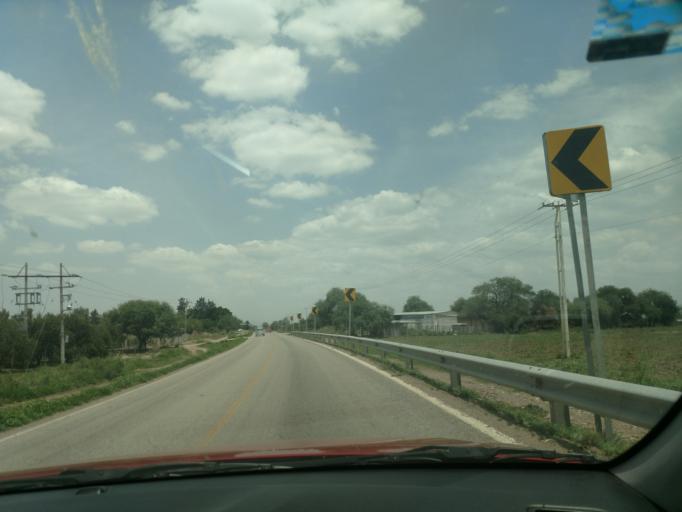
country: MX
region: San Luis Potosi
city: Ciudad Fernandez
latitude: 21.9505
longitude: -100.0634
